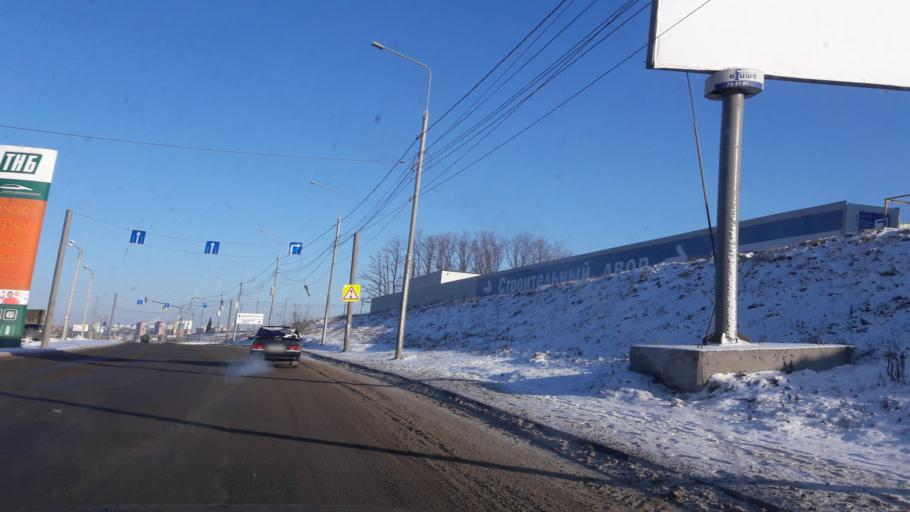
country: RU
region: Tula
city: Tula
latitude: 54.1742
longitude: 37.6421
